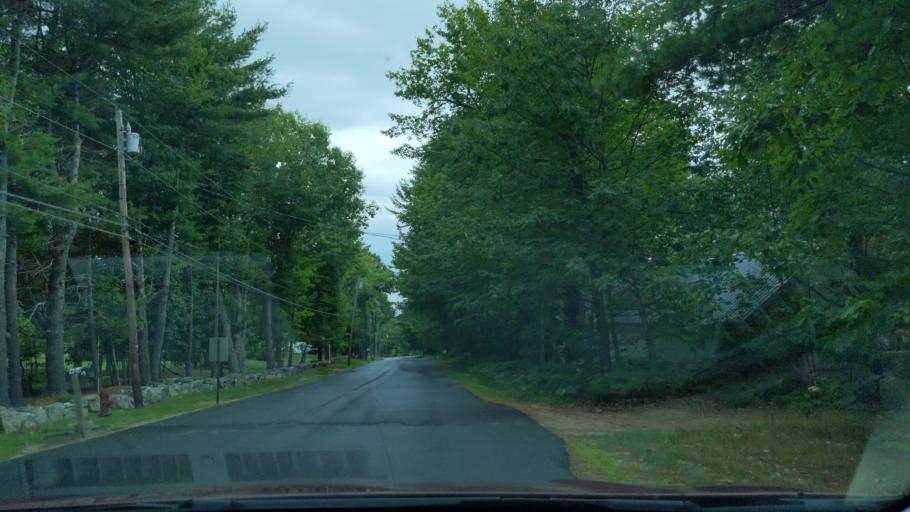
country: US
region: New Hampshire
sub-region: Merrimack County
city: New London
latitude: 43.4197
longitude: -72.0232
